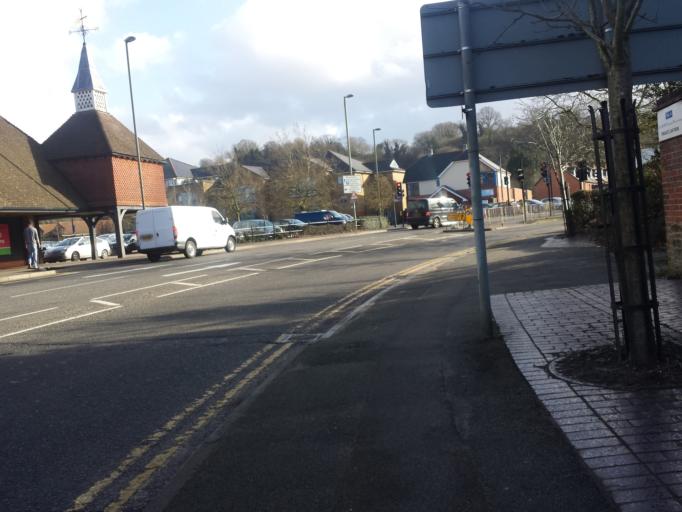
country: GB
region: England
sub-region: Surrey
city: Godalming
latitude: 51.1871
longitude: -0.6080
